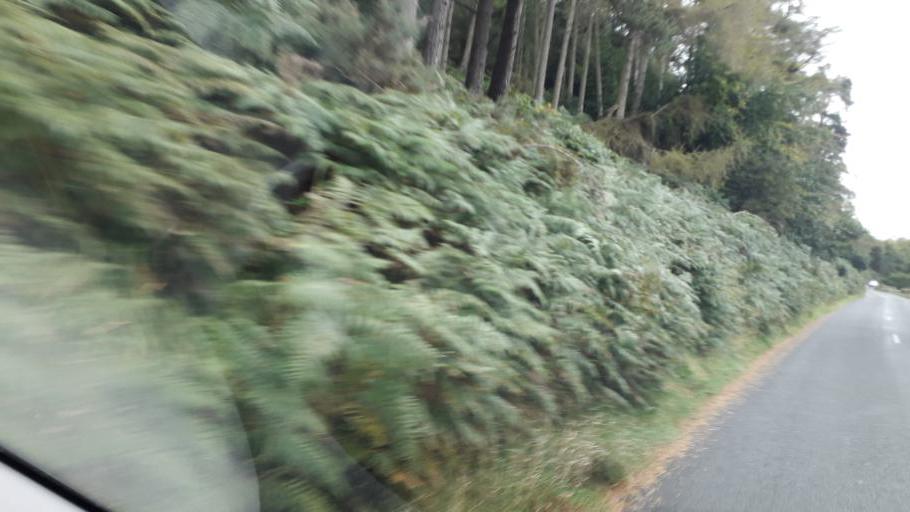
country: IE
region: Leinster
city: Ballyboden
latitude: 53.2418
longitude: -6.2919
